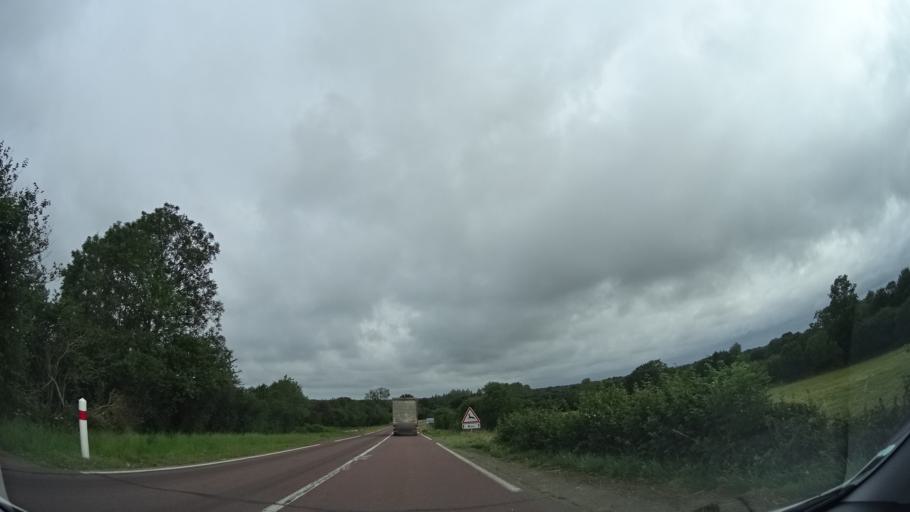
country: FR
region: Lower Normandy
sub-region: Departement de la Manche
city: Pirou
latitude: 49.1347
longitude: -1.5043
